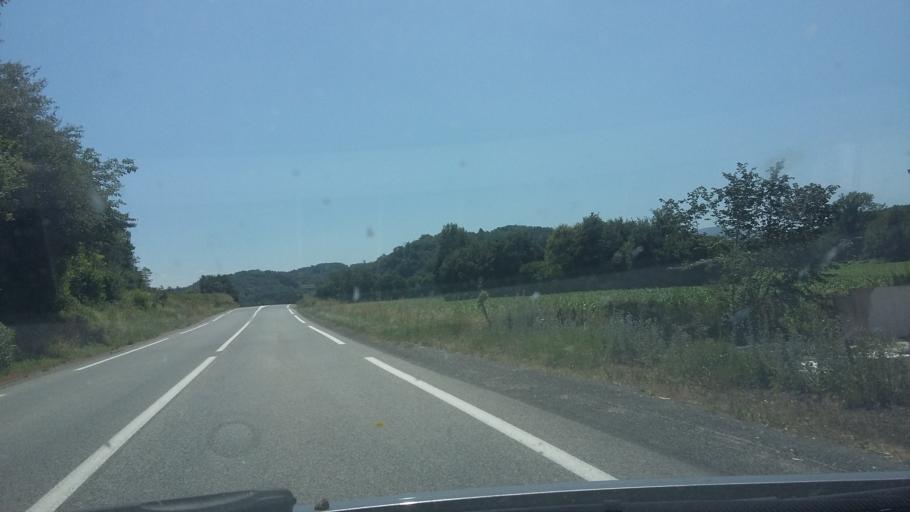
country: FR
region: Rhone-Alpes
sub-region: Departement de l'Ain
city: Belley
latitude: 45.7959
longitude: 5.6825
